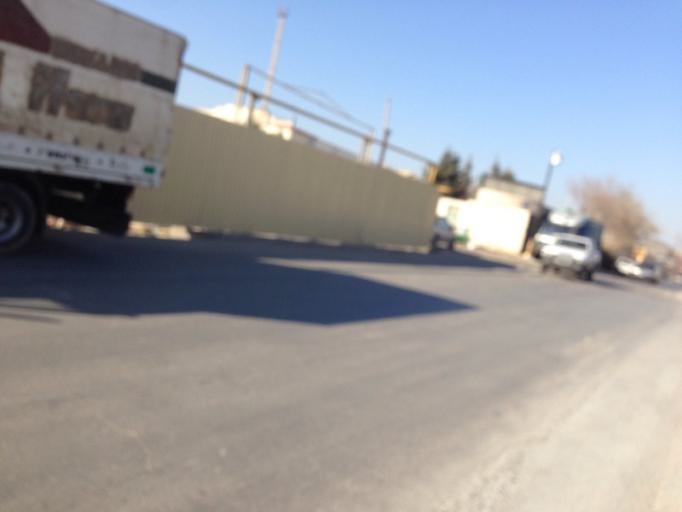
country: AZ
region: Baki
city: Baku
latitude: 40.4199
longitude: 49.8655
